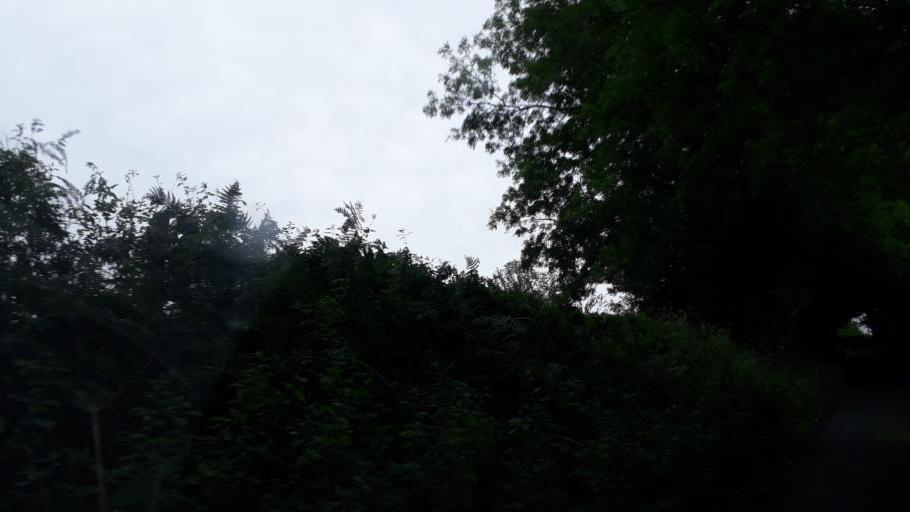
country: IE
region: Leinster
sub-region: Wicklow
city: Enniskerry
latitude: 53.1682
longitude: -6.1992
